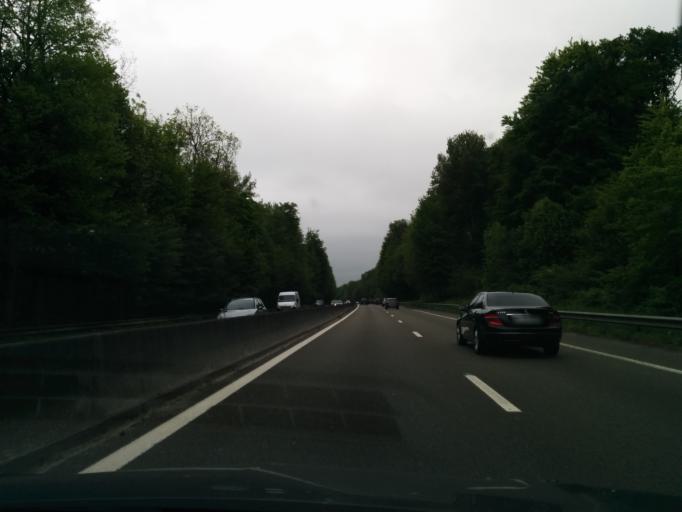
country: FR
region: Ile-de-France
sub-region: Departement des Yvelines
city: Saint-Nom-la-Breteche
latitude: 48.8854
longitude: 2.0128
